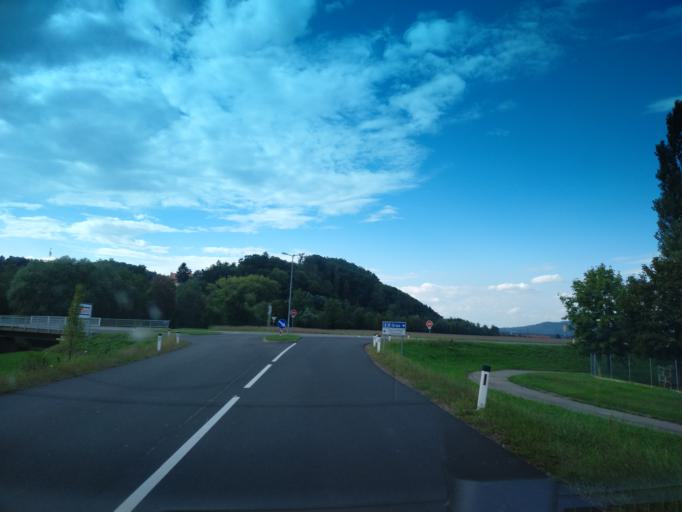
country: AT
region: Styria
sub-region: Politischer Bezirk Leibnitz
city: Kaindorf an der Sulm
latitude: 46.7944
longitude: 15.5313
